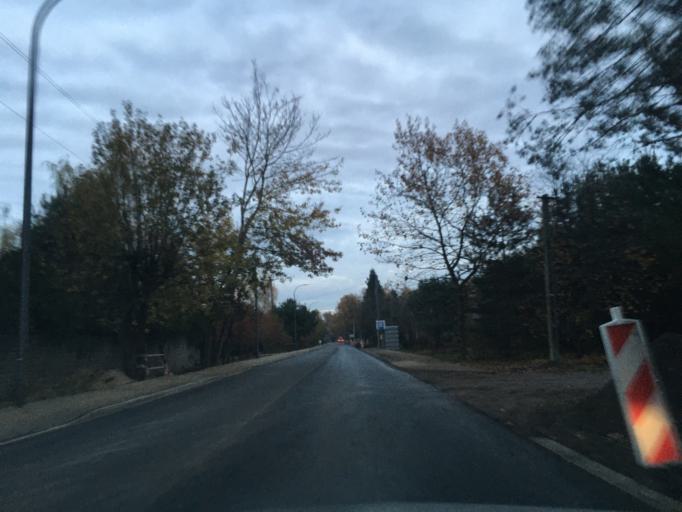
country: PL
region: Masovian Voivodeship
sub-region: Powiat piaseczynski
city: Lesznowola
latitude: 52.0584
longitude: 20.9745
